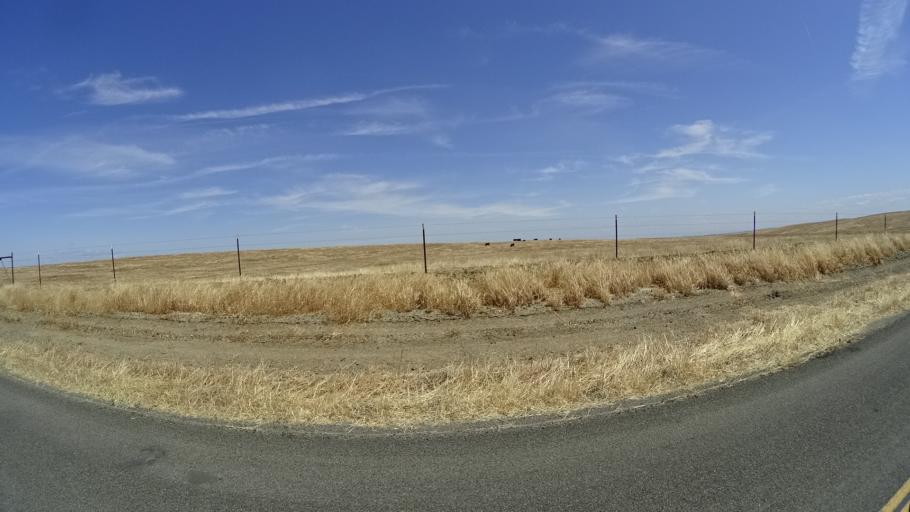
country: US
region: California
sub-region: Kings County
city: Kettleman City
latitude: 35.8254
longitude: -119.9098
